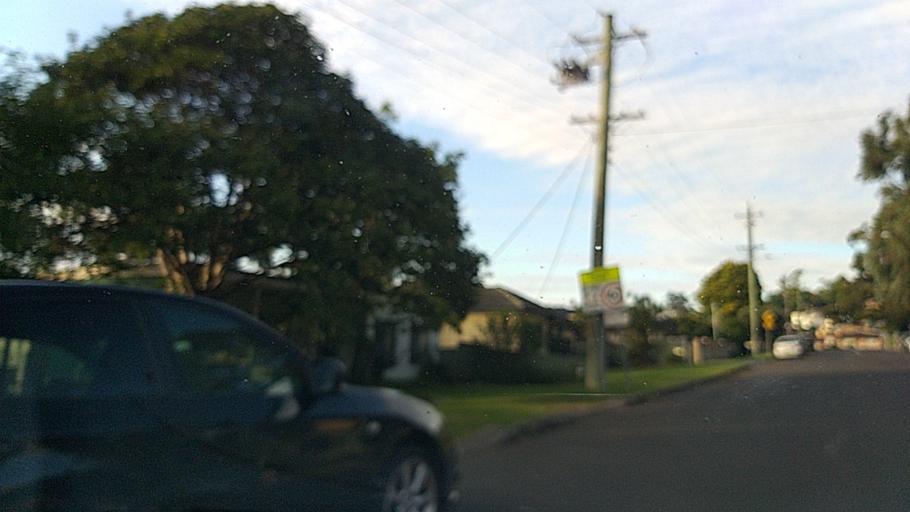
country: AU
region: New South Wales
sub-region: Wollongong
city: Mount Ousley
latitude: -34.3861
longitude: 150.8731
